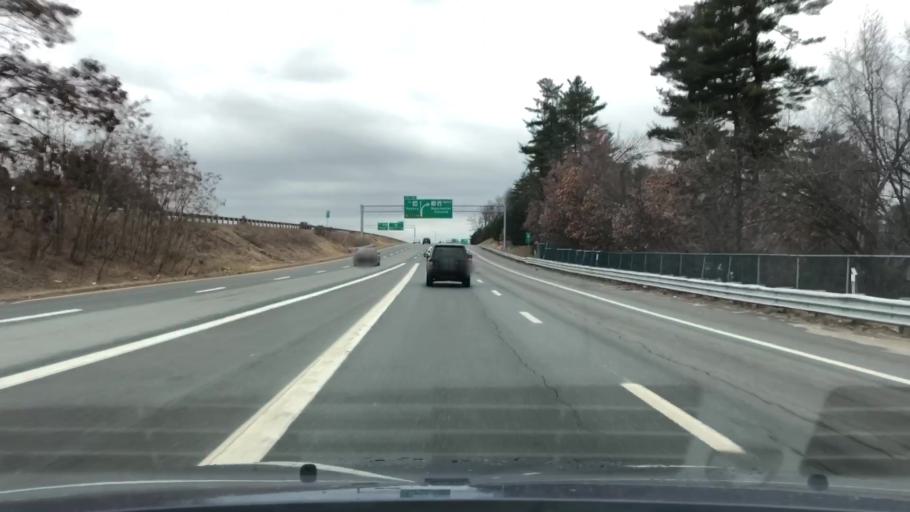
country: US
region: Massachusetts
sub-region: Middlesex County
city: Tyngsboro
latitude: 42.7104
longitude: -71.4499
